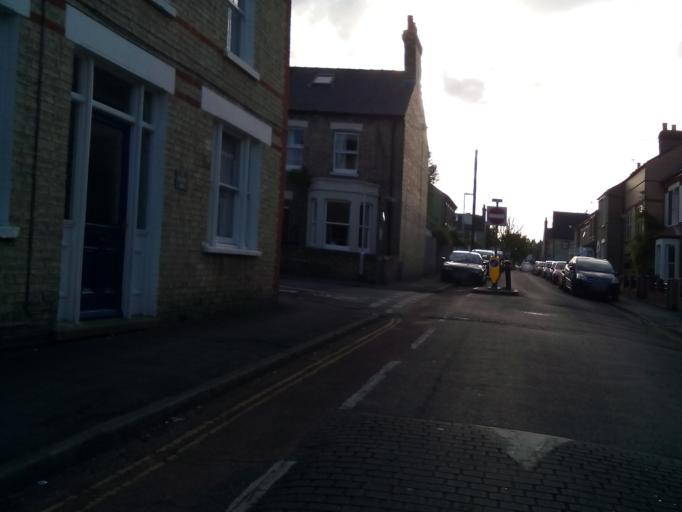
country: GB
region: England
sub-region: Cambridgeshire
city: Cambridge
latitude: 52.1984
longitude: 0.1507
